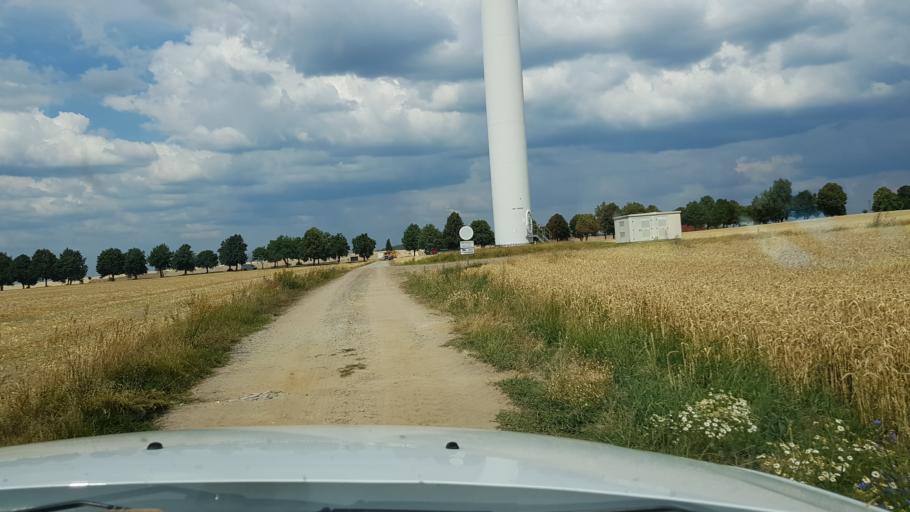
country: PL
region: West Pomeranian Voivodeship
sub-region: Powiat walecki
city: Walcz
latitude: 53.2512
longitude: 16.5153
